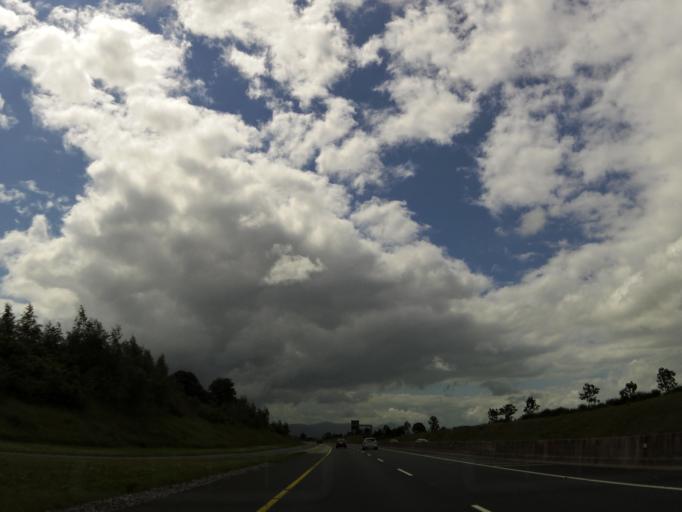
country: IE
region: Munster
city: Cashel
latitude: 52.4954
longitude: -7.8919
